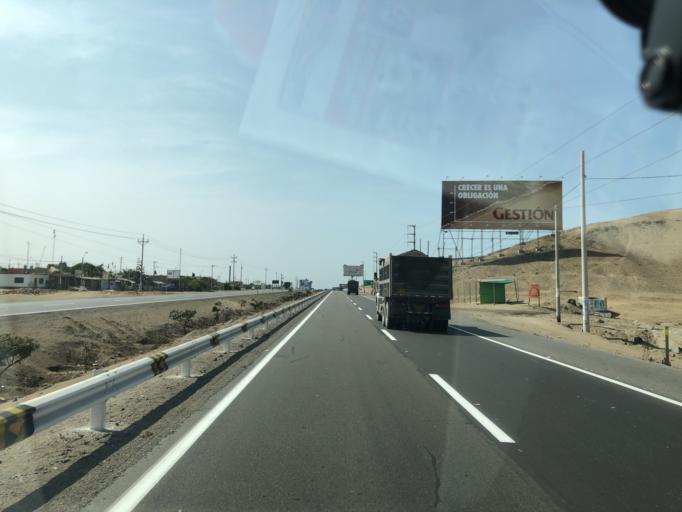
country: PE
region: Lima
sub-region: Provincia de Canete
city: Asia
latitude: -12.7341
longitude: -76.6149
